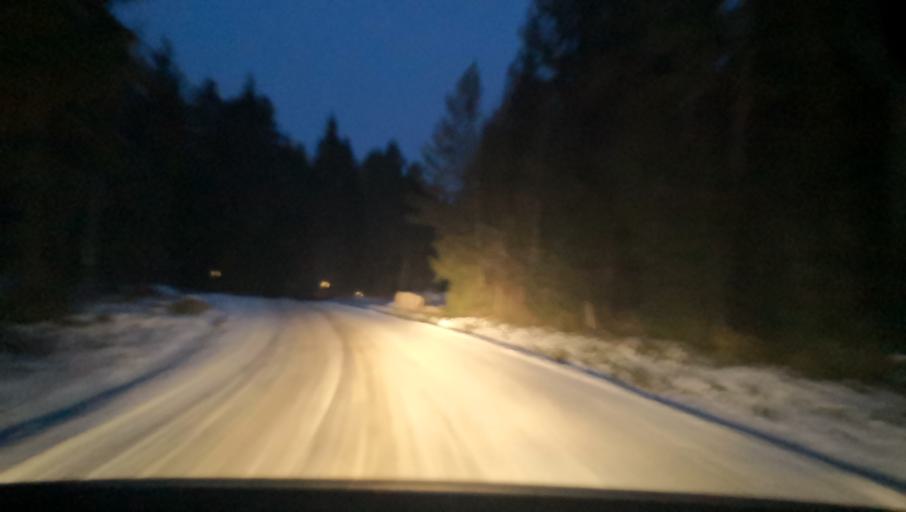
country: SE
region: Uppsala
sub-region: Heby Kommun
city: Tarnsjo
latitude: 60.2524
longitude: 16.7353
